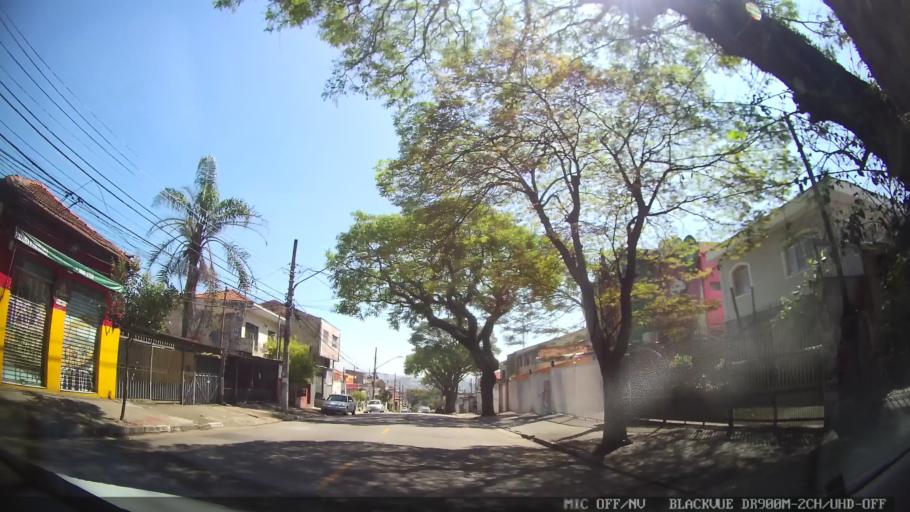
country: BR
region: Sao Paulo
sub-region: Sao Paulo
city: Sao Paulo
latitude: -23.5006
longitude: -46.6526
